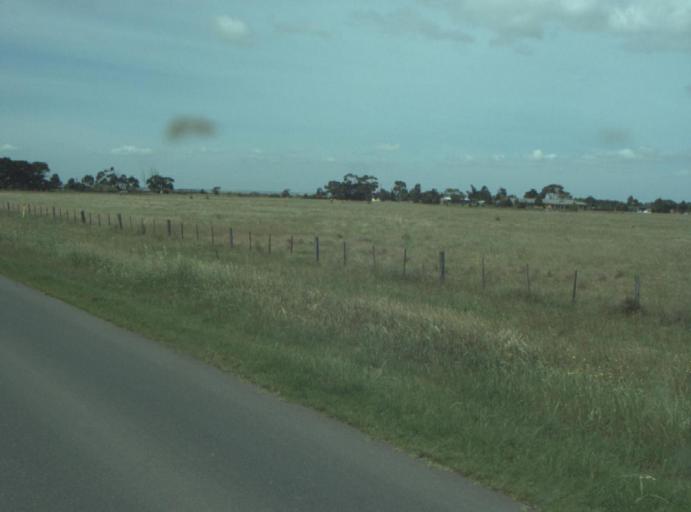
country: AU
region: Victoria
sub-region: Wyndham
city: Little River
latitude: -38.0088
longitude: 144.4630
